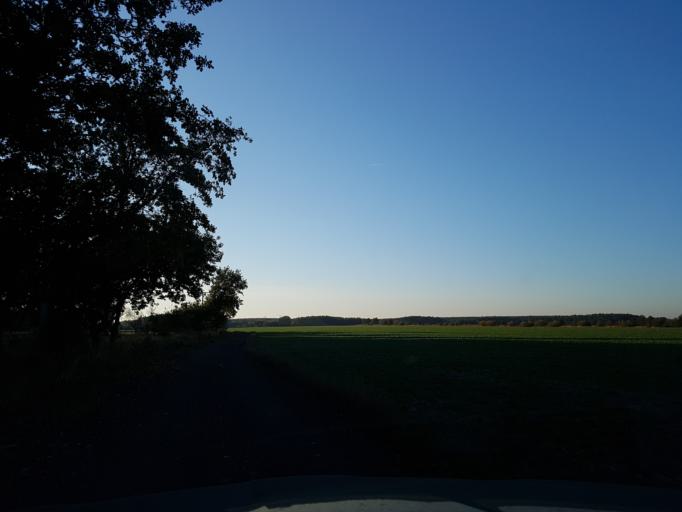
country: DE
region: Brandenburg
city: Bad Liebenwerda
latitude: 51.5453
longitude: 13.3996
